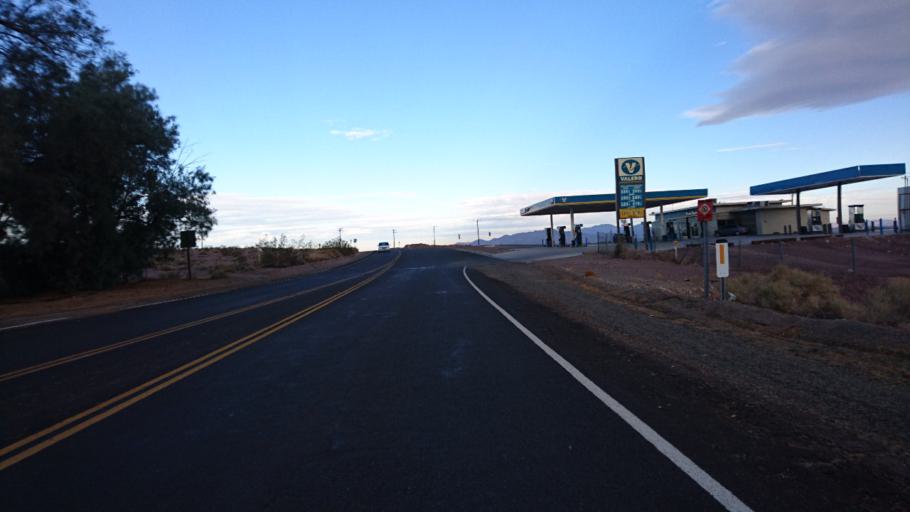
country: US
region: California
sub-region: San Bernardino County
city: Barstow
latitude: 34.8308
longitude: -116.6954
